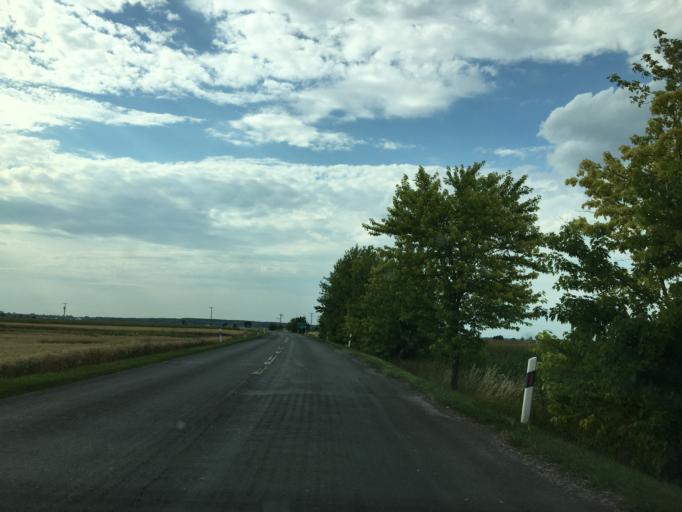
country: HU
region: Bacs-Kiskun
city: Dusnok
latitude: 46.4159
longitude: 18.9466
